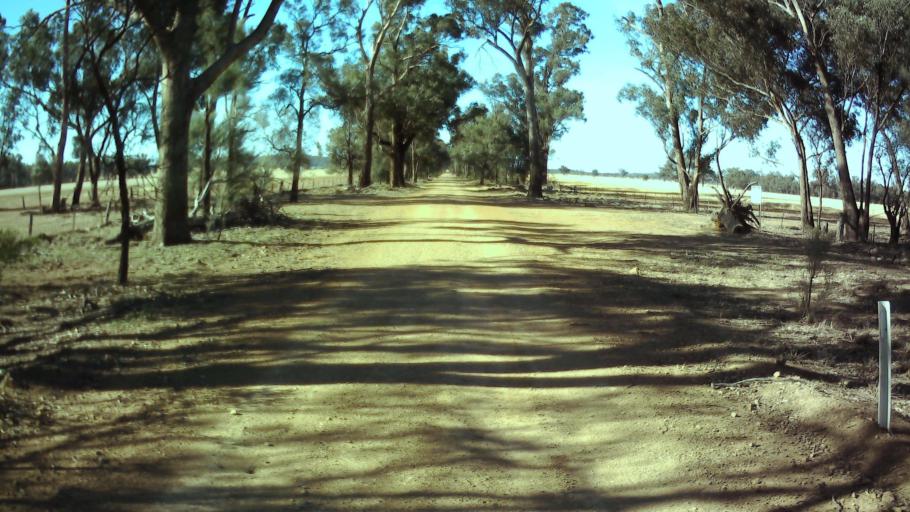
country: AU
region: New South Wales
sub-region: Weddin
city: Grenfell
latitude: -33.8306
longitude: 147.8736
